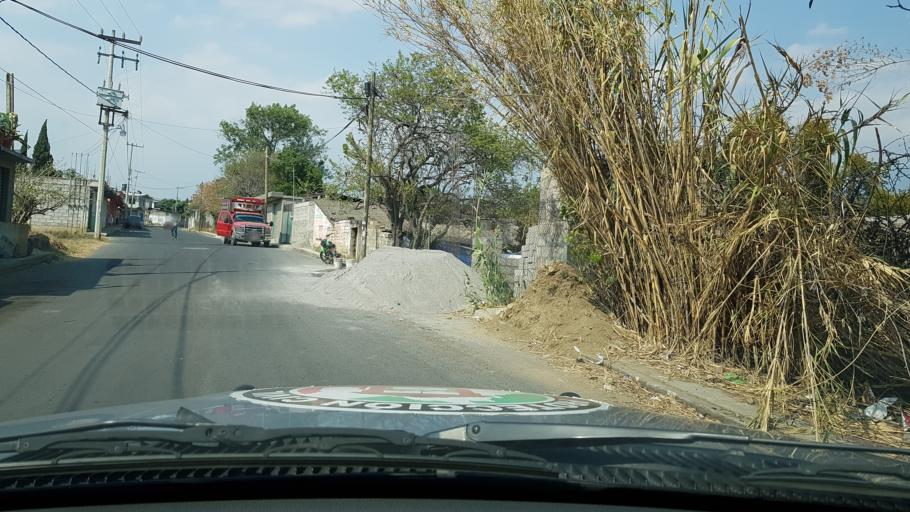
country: MX
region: Mexico
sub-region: Ozumba
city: San Jose Tlacotitlan
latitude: 18.9810
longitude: -98.8099
